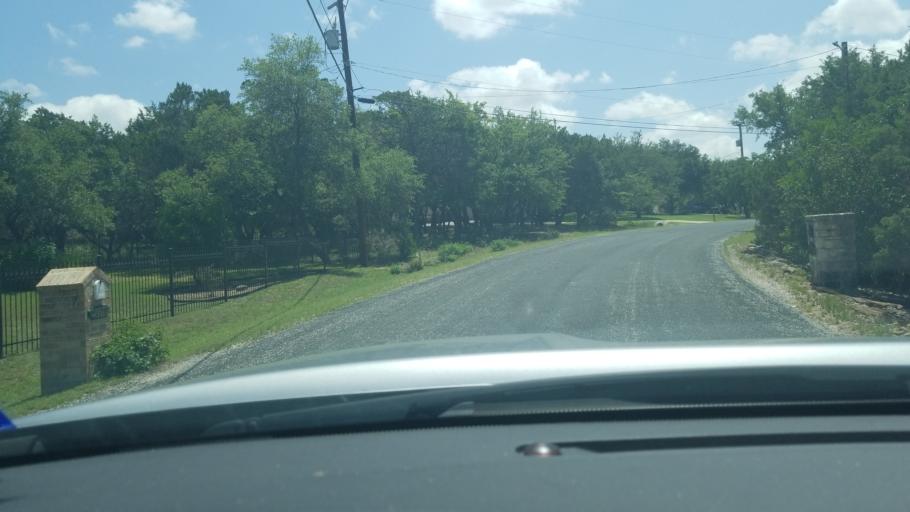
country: US
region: Texas
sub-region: Bexar County
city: Timberwood Park
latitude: 29.6918
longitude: -98.4879
